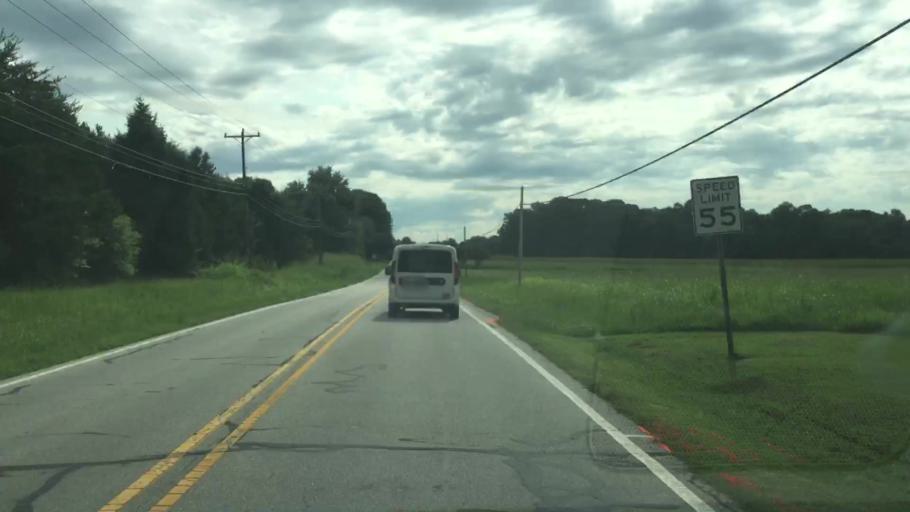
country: US
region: North Carolina
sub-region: Rowan County
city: Franklin
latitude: 35.6612
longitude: -80.5596
